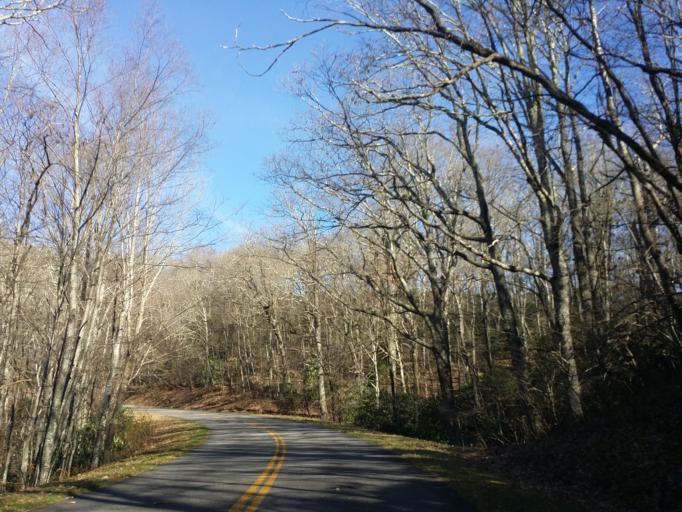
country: US
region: North Carolina
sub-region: Mitchell County
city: Spruce Pine
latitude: 35.7794
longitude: -82.1595
